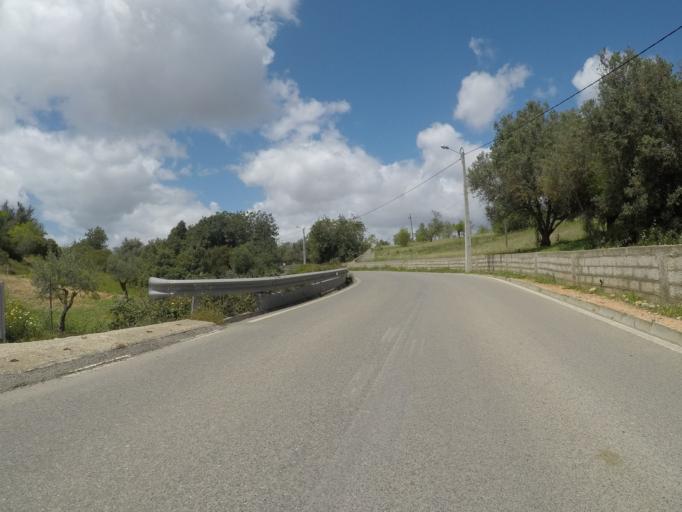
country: PT
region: Faro
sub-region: Lagoa
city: Lagoa
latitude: 37.1167
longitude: -8.4109
